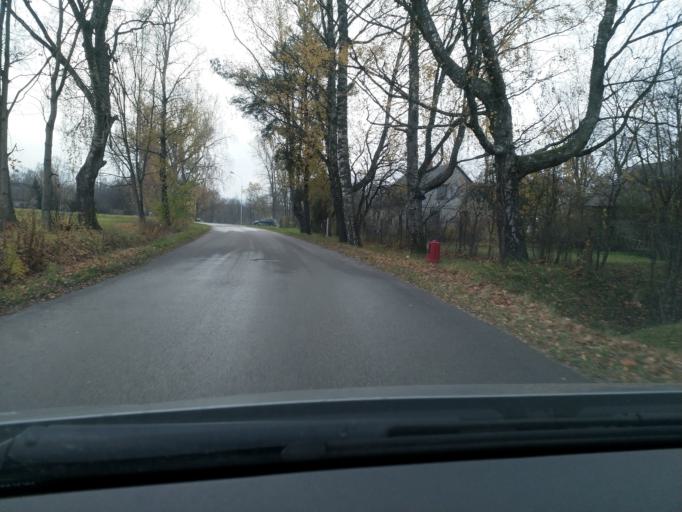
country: LV
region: Kuldigas Rajons
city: Kuldiga
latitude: 56.9748
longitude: 21.9778
